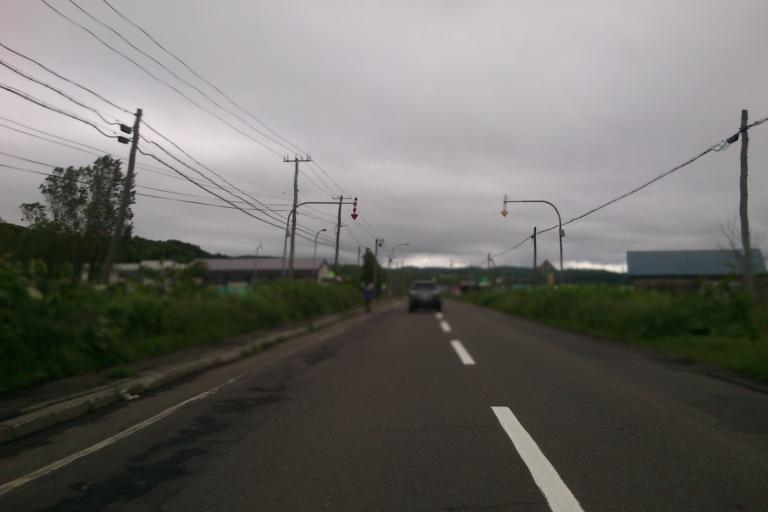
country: JP
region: Hokkaido
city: Ishikari
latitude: 43.3172
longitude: 141.4258
